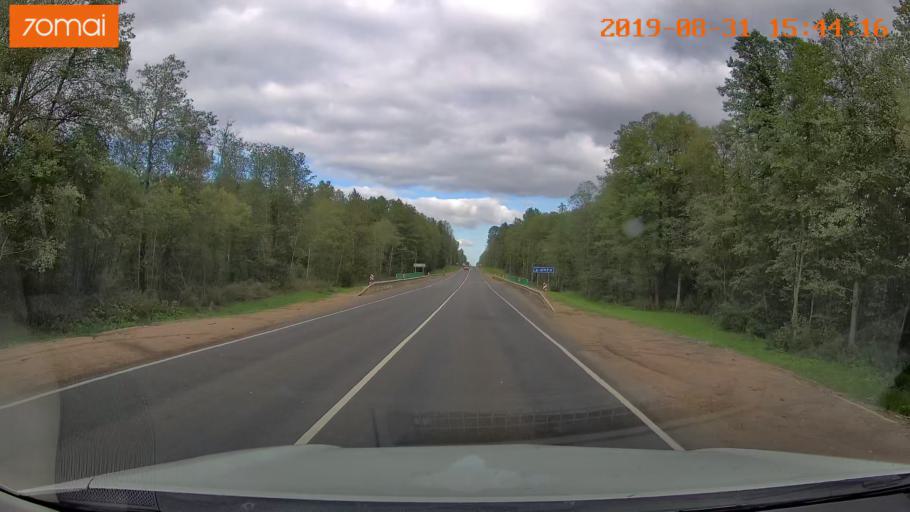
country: RU
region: Kaluga
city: Mosal'sk
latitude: 54.6579
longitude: 34.9288
